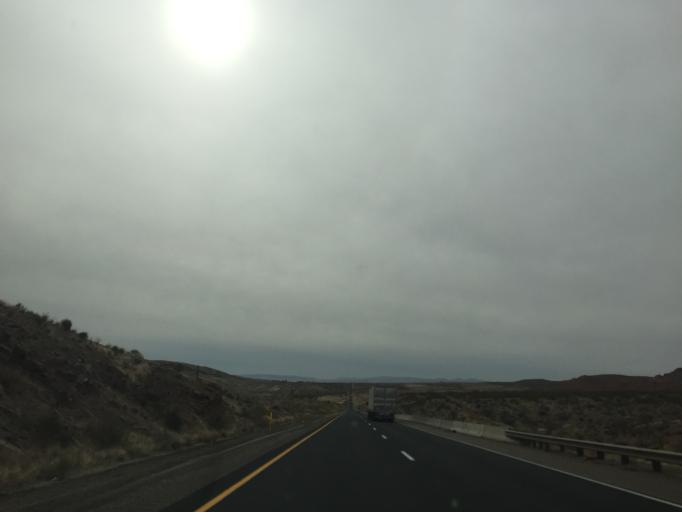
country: US
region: Utah
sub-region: Washington County
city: Hurricane
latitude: 37.2148
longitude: -113.3903
